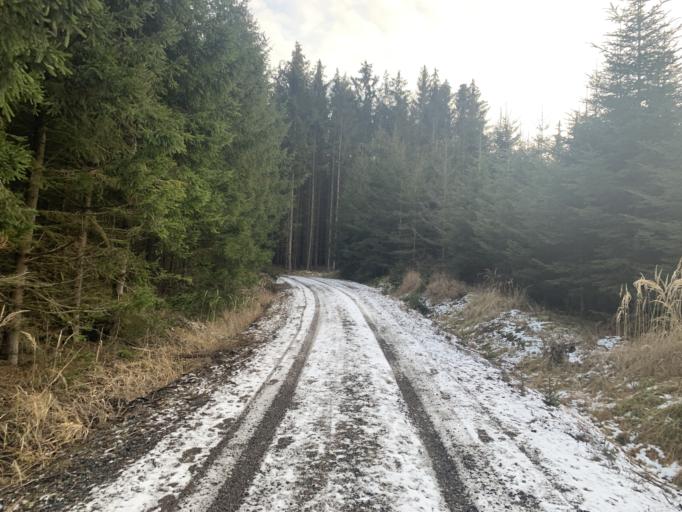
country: CZ
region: Plzensky
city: Zbiroh
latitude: 49.8216
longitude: 13.7981
